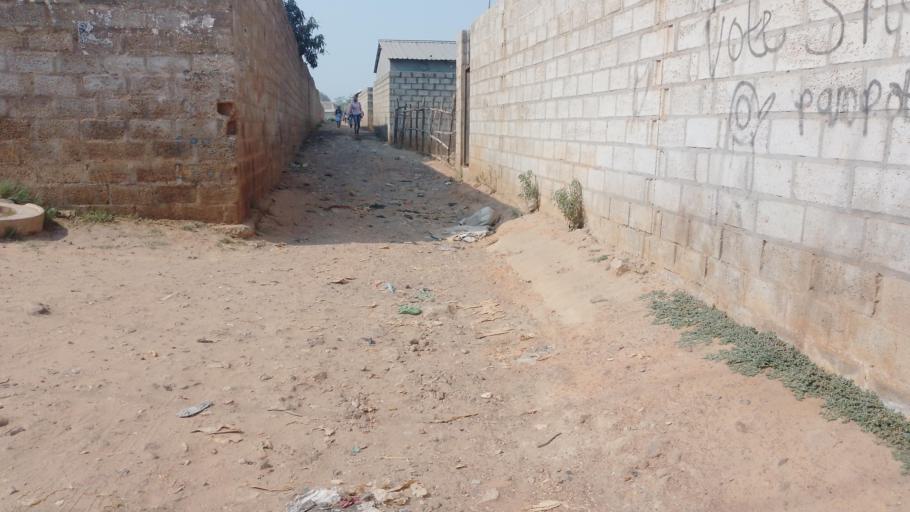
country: ZM
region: Lusaka
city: Lusaka
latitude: -15.3995
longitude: 28.3659
